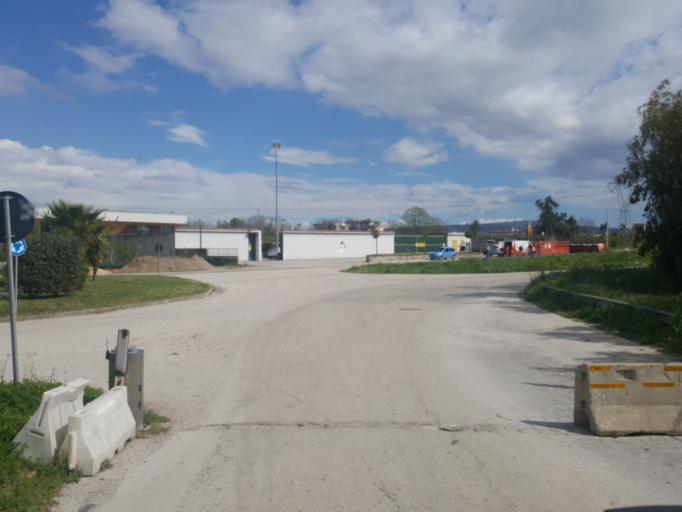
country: IT
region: Campania
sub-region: Provincia di Napoli
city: Torretta-Scalzapecora
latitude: 40.9340
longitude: 14.1218
